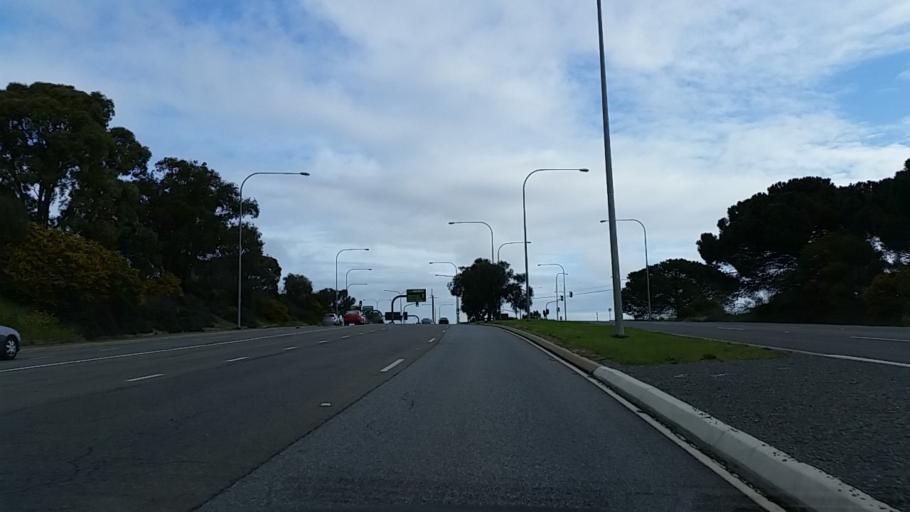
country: AU
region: South Australia
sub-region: Marion
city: Trott Park
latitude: -35.0795
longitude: 138.5474
